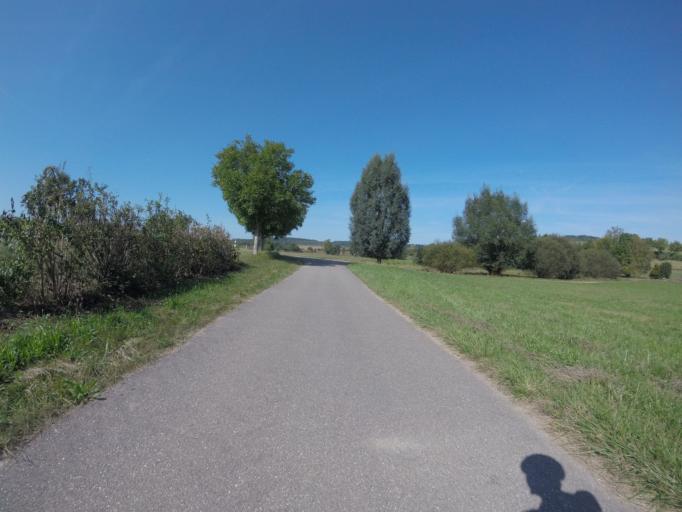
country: DE
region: Baden-Wuerttemberg
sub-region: Regierungsbezirk Stuttgart
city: Grossbottwar
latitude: 49.0103
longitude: 9.2768
